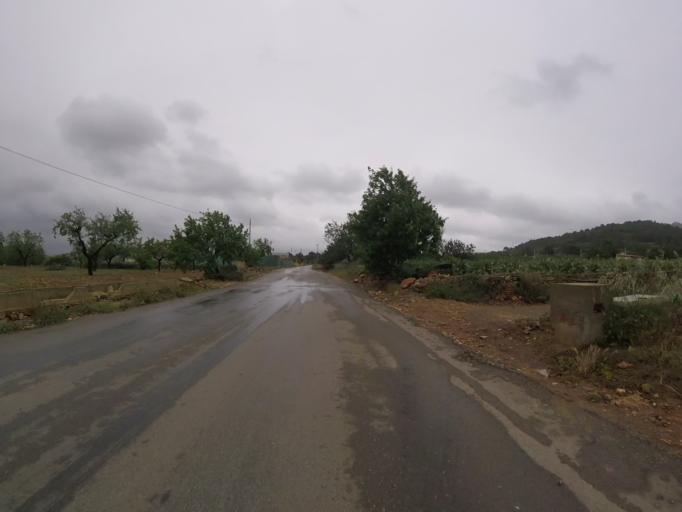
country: ES
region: Valencia
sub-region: Provincia de Castello
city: Alcoceber
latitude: 40.2469
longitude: 0.2467
